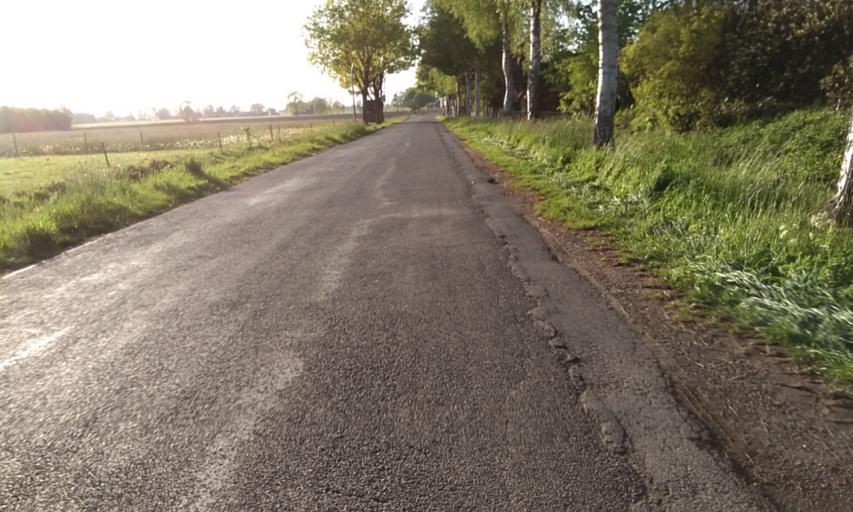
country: DE
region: Lower Saxony
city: Wohnste
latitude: 53.3948
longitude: 9.5054
